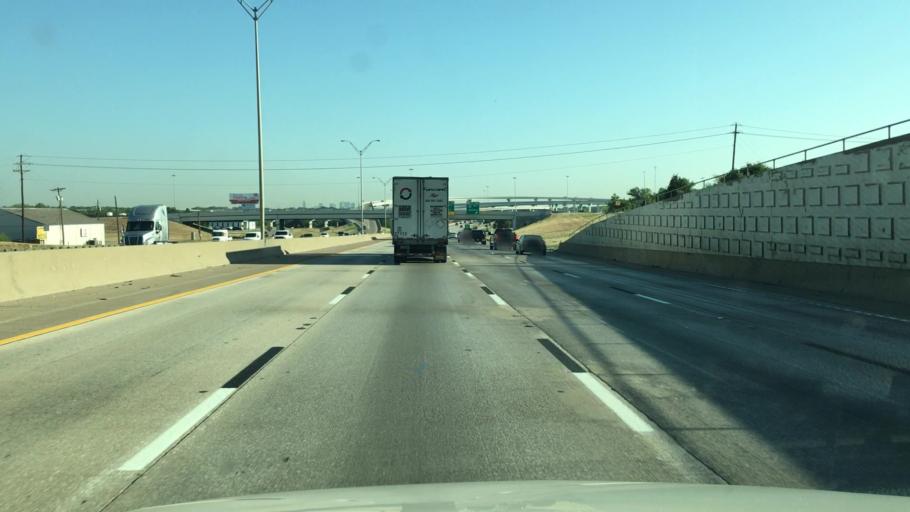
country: US
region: Texas
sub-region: Tarrant County
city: Edgecliff Village
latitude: 32.6580
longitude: -97.3212
